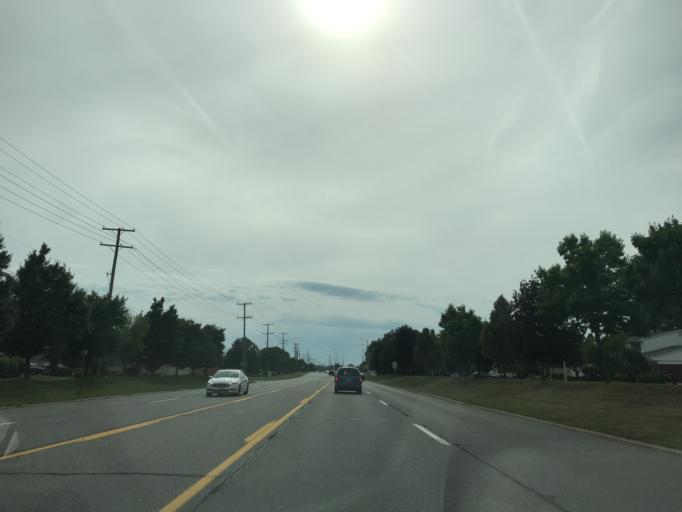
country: US
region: Michigan
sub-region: Oakland County
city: Farmington
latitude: 42.4111
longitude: -83.4064
